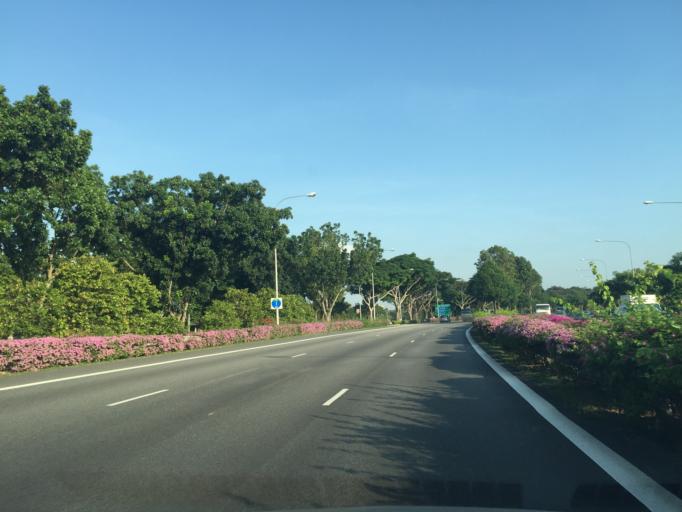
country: SG
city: Singapore
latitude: 1.3403
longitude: 103.9720
